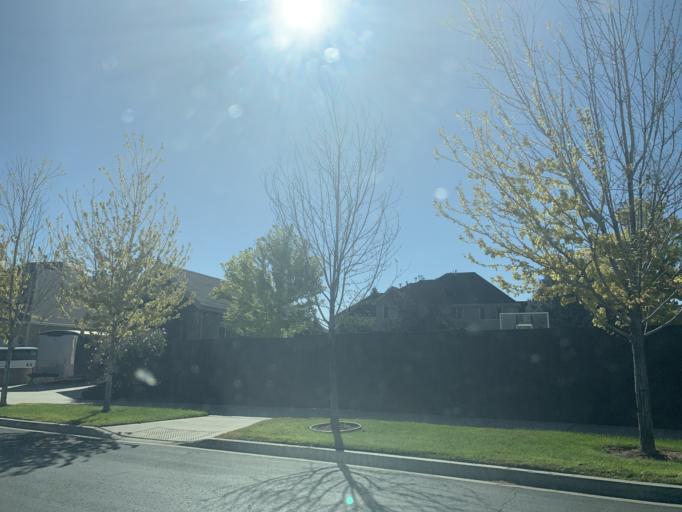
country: US
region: Utah
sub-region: Utah County
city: Provo
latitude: 40.2579
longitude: -111.6888
